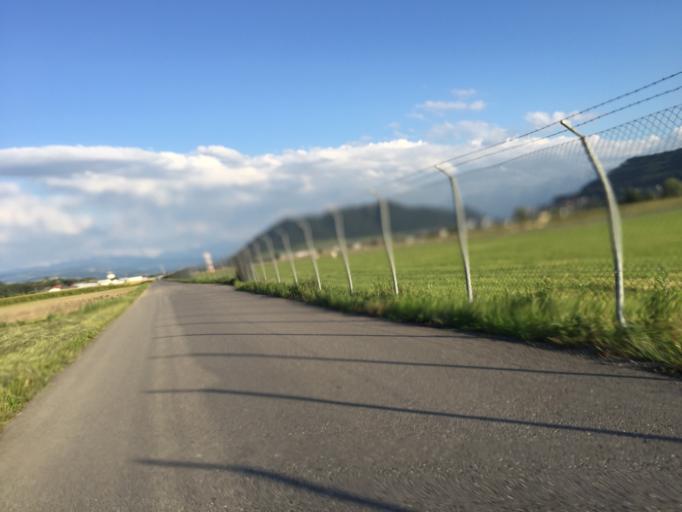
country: CH
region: Bern
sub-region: Bern-Mittelland District
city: Muri
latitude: 46.9195
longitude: 7.4918
